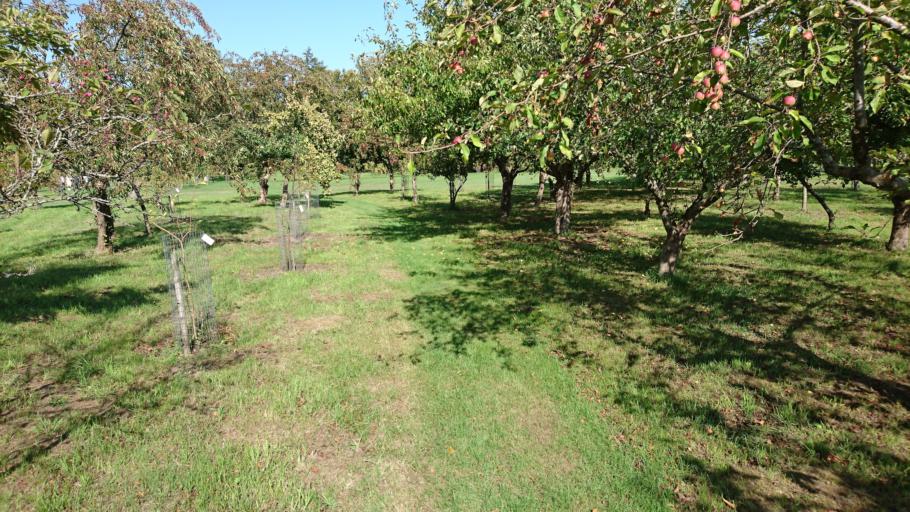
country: DK
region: North Denmark
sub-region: Frederikshavn Kommune
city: Saeby
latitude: 57.3437
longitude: 10.5055
